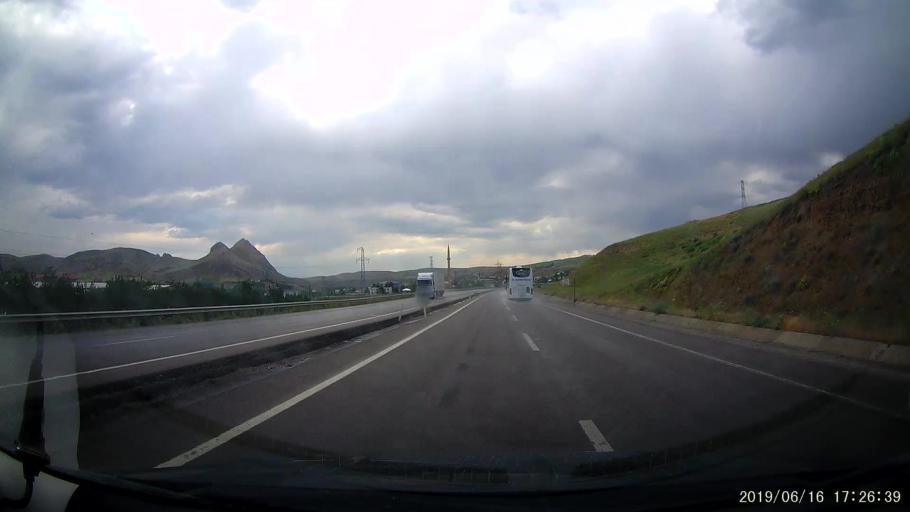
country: TR
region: Erzincan
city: Tercan
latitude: 39.7700
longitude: 40.4077
